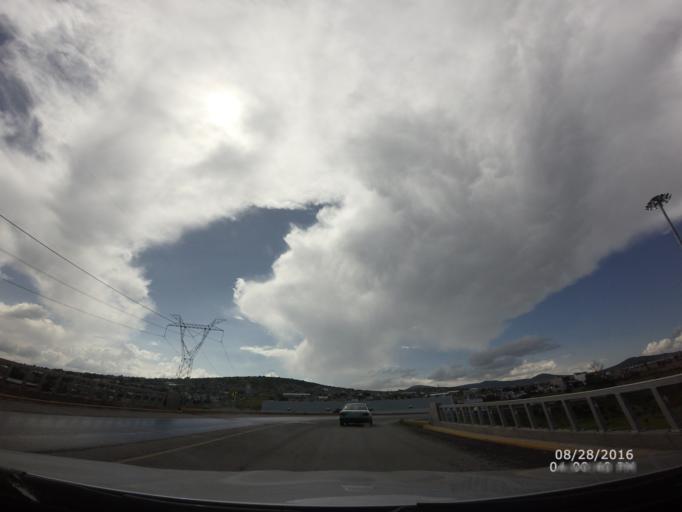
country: MX
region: Hidalgo
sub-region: Zempoala
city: Lindavista
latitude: 20.0402
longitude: -98.7957
